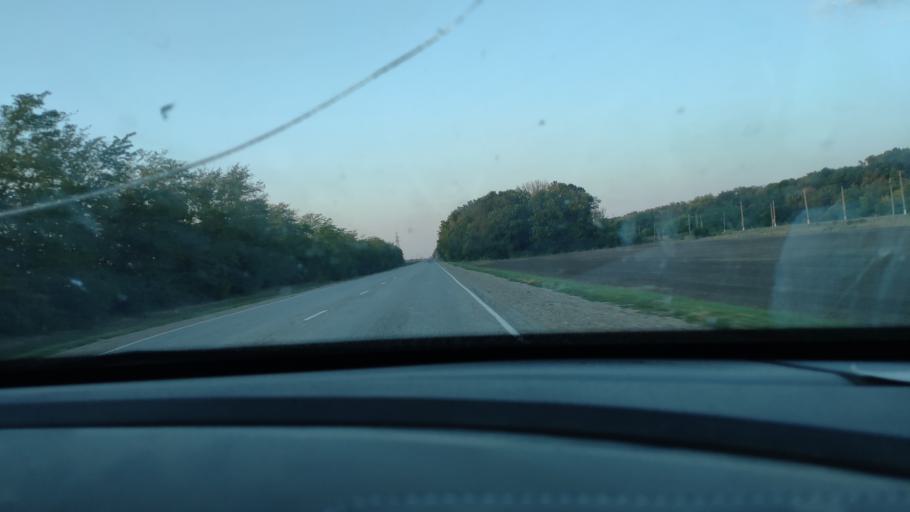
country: RU
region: Krasnodarskiy
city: Starominskaya
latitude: 46.4832
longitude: 39.0533
